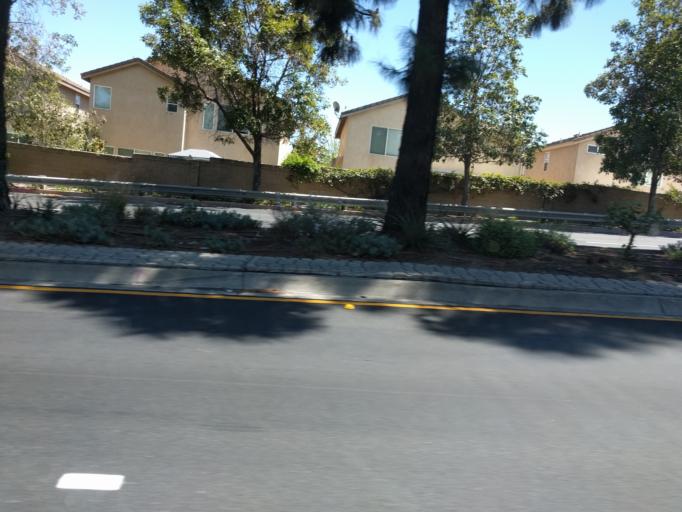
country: US
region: California
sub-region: San Diego County
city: Poway
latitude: 32.9406
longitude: -117.1148
